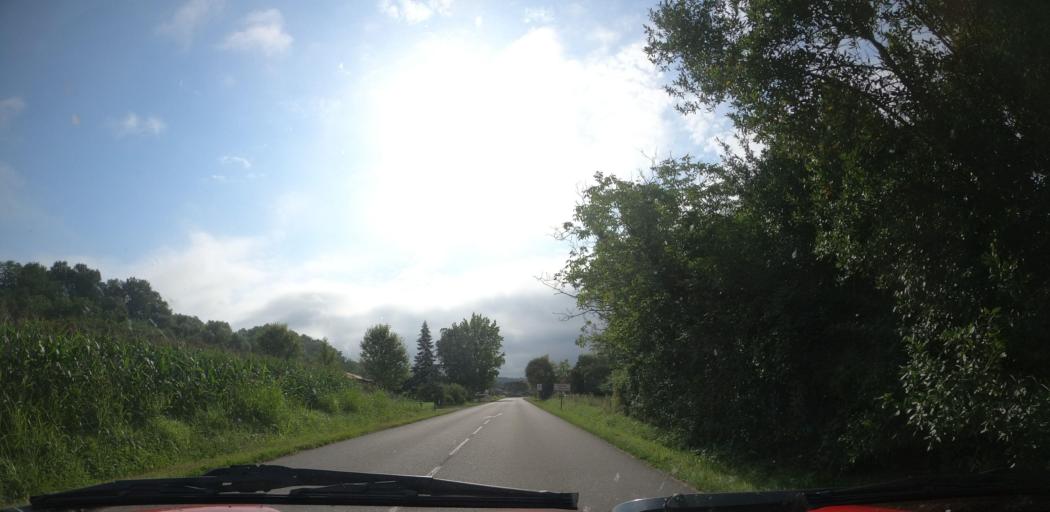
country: FR
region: Aquitaine
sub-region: Departement des Landes
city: Peyrehorade
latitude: 43.5324
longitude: -1.0647
